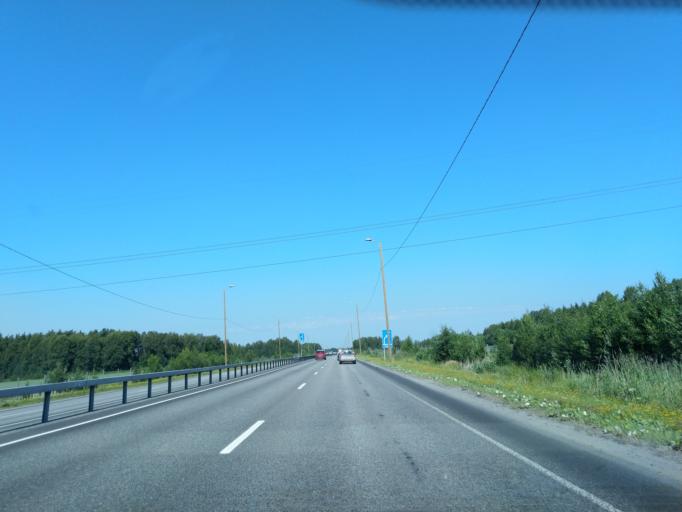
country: FI
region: Satakunta
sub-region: Pori
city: Nakkila
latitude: 61.3404
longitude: 22.0374
